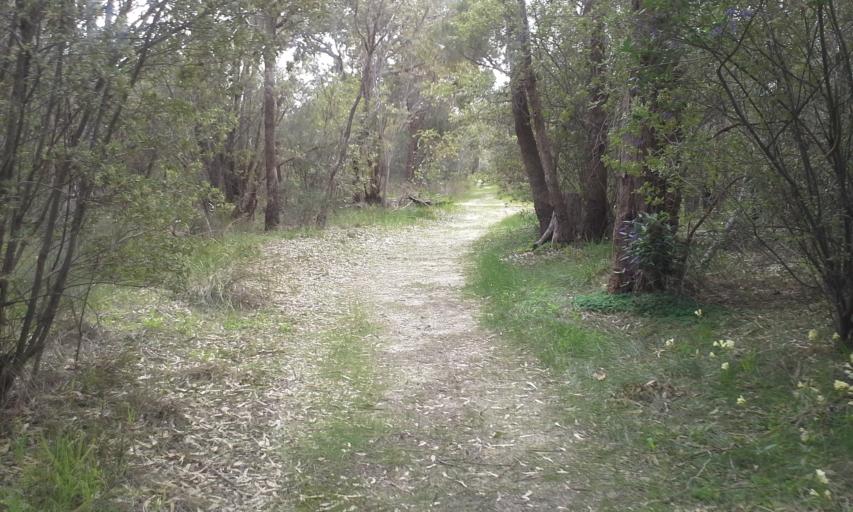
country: AU
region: Western Australia
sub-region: City of Perth
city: West Perth
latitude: -31.9591
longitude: 115.8347
